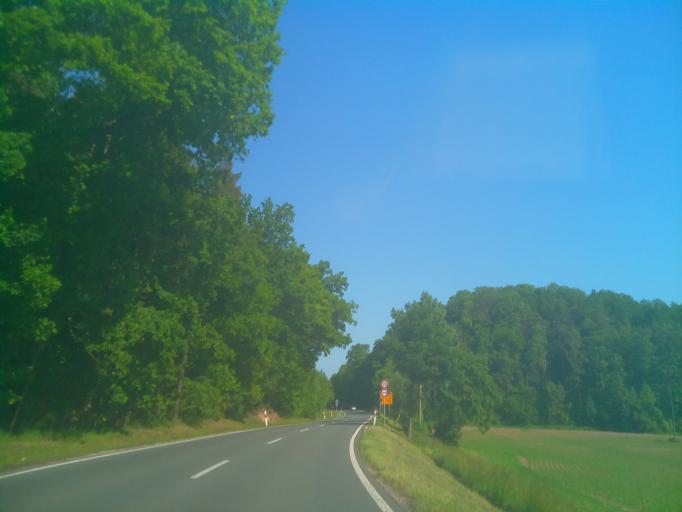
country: DE
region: Thuringia
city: Bad Blankenburg
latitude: 50.6956
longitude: 11.2230
